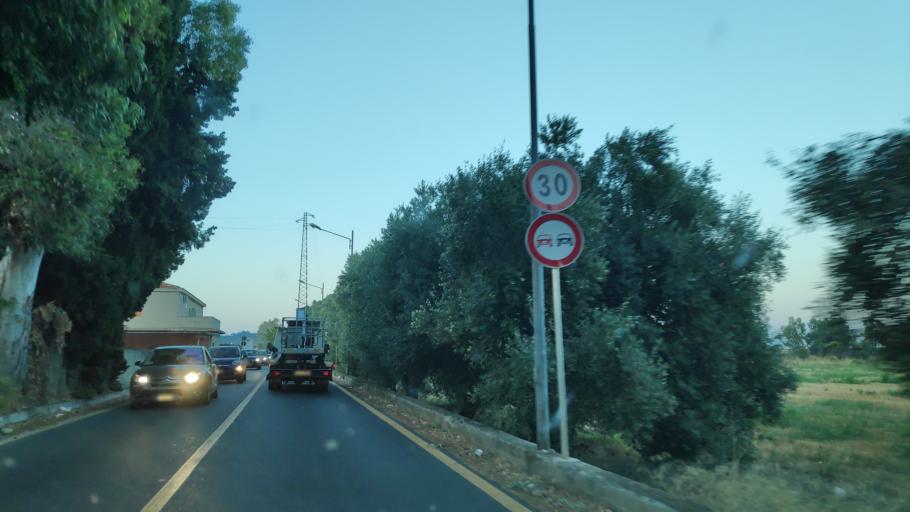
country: IT
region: Calabria
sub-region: Provincia di Reggio Calabria
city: Caulonia Marina
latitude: 38.3476
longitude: 16.4691
